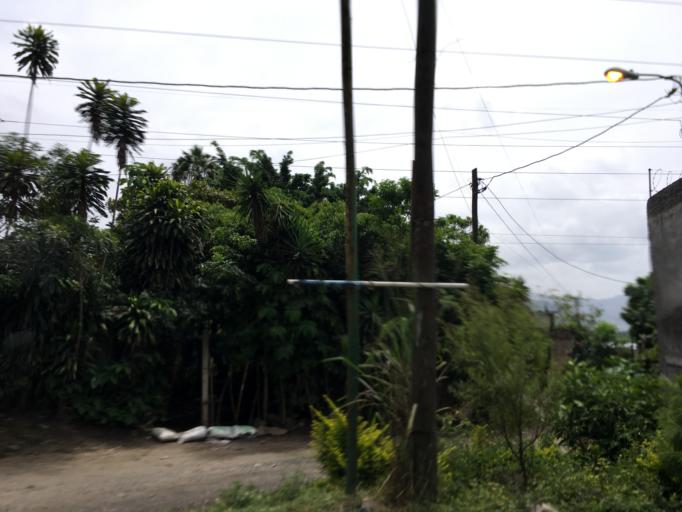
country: GT
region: Guatemala
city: Amatitlan
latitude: 14.4597
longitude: -90.5758
